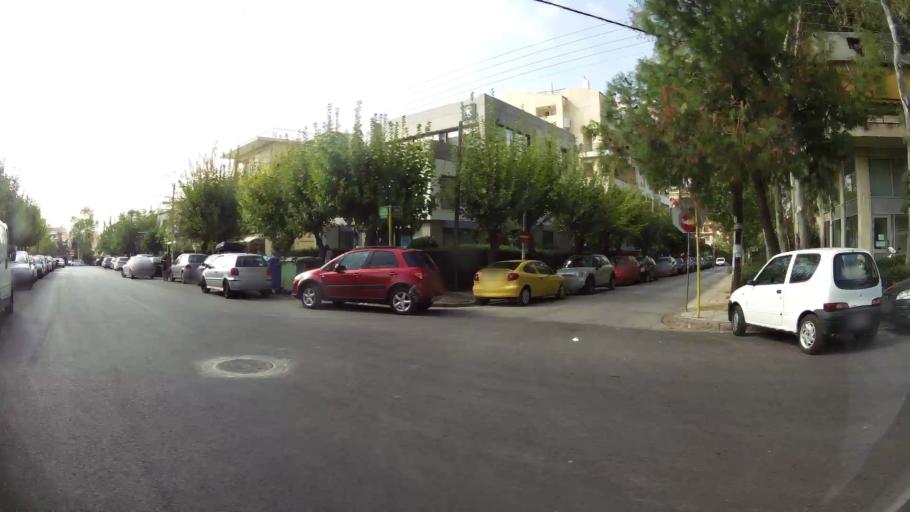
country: GR
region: Attica
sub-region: Nomarchia Athinas
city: Cholargos
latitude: 37.9932
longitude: 23.7993
